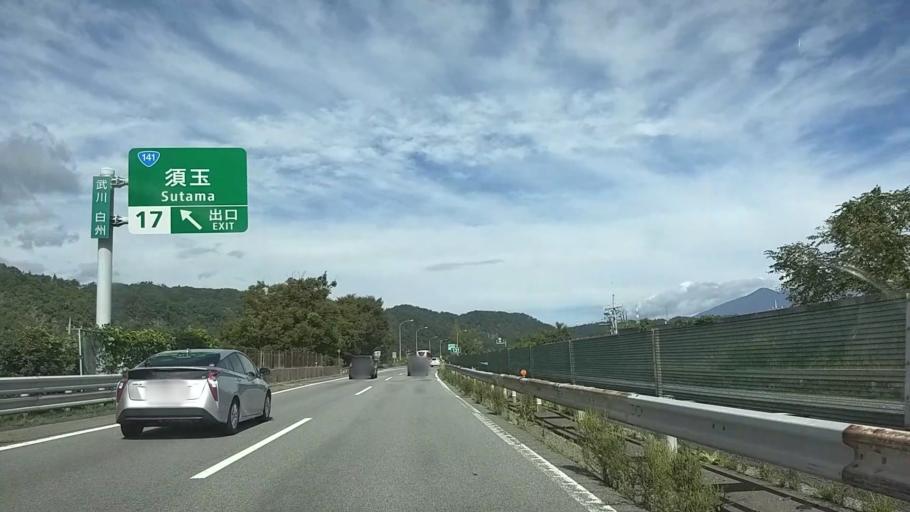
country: JP
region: Yamanashi
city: Nirasaki
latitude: 35.7696
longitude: 138.4271
